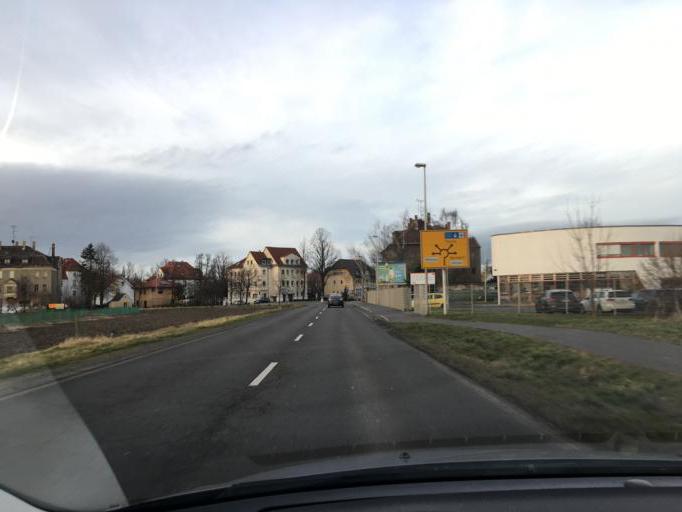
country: DE
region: Saxony
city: Taucha
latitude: 51.3315
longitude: 12.4810
